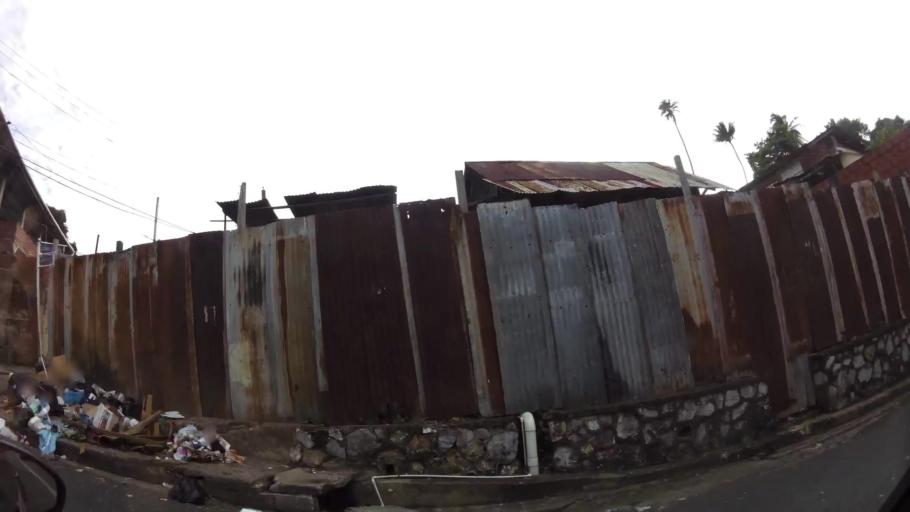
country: TT
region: San Juan/Laventille
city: Laventille
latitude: 10.6556
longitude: -61.5020
